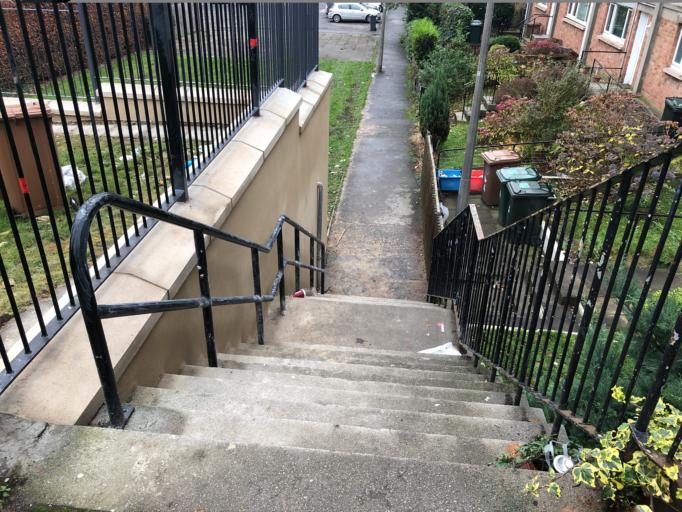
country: GB
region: Scotland
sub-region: West Lothian
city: Seafield
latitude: 55.9479
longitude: -3.1355
